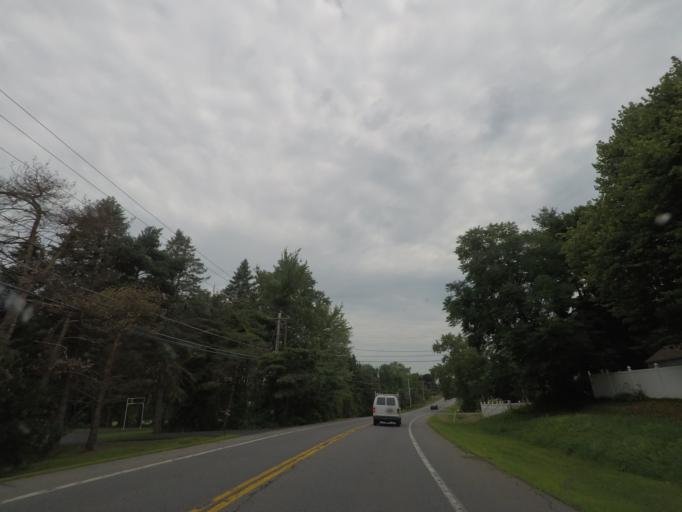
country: US
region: New York
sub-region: Saratoga County
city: Waterford
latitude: 42.8061
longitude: -73.6845
